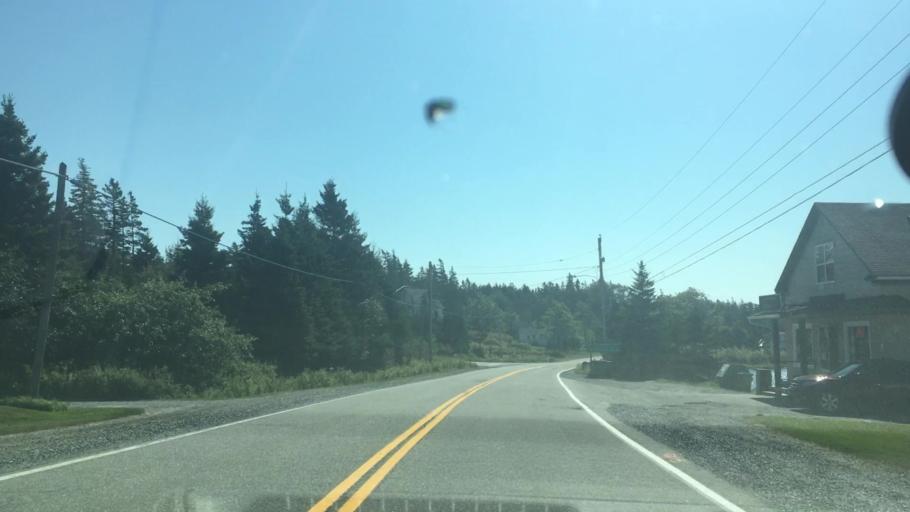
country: CA
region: Nova Scotia
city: New Glasgow
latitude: 44.9164
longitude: -62.3824
